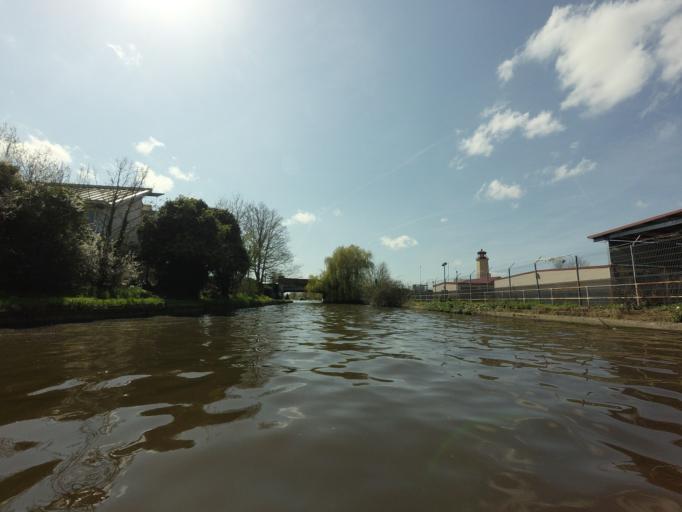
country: GB
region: England
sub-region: Greater London
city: Southall
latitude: 51.5139
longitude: -0.3899
